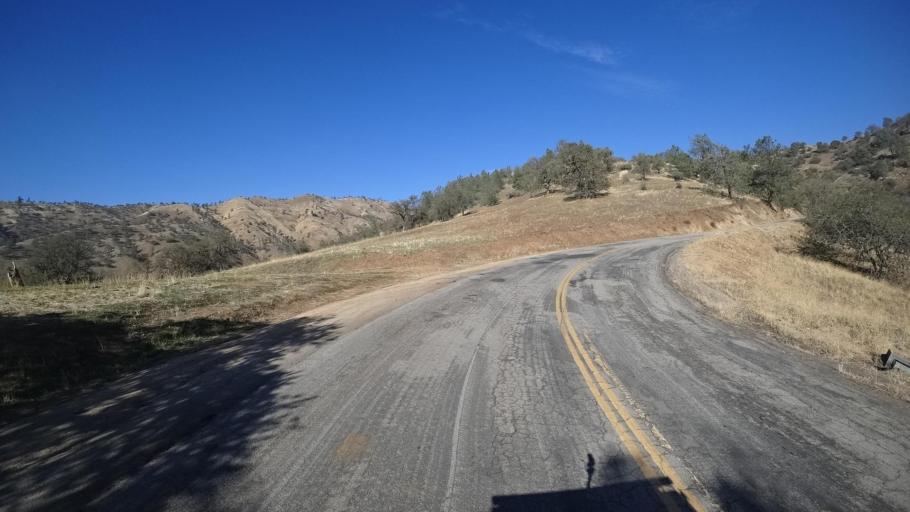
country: US
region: California
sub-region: Kern County
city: Bear Valley Springs
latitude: 35.3312
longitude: -118.5858
